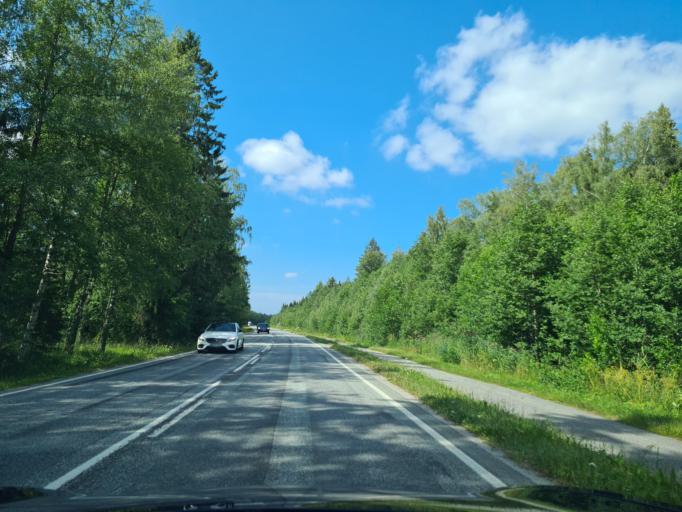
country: FI
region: Ostrobothnia
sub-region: Vaasa
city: Vaasa
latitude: 63.1970
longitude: 21.5431
